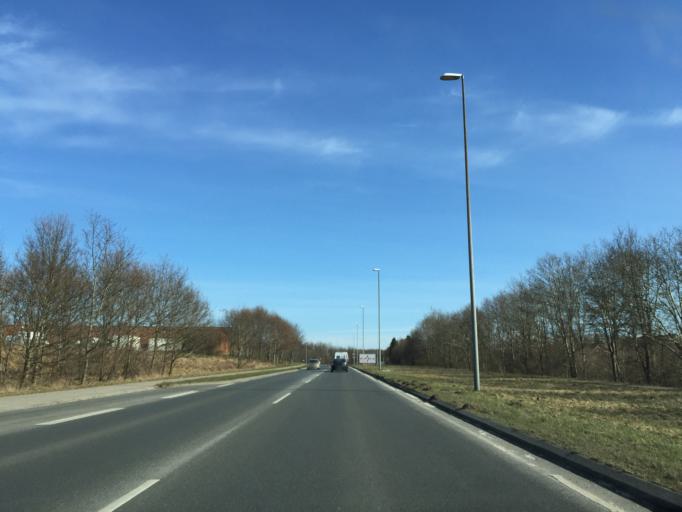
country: DK
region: Central Jutland
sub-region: Silkeborg Kommune
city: Silkeborg
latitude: 56.1994
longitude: 9.5875
